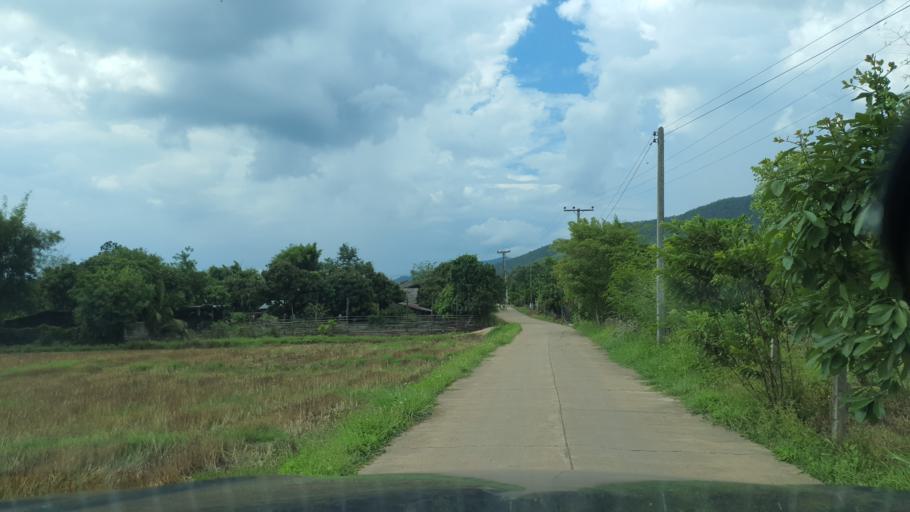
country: TH
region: Chiang Mai
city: Mae Taeng
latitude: 19.1381
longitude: 99.0365
